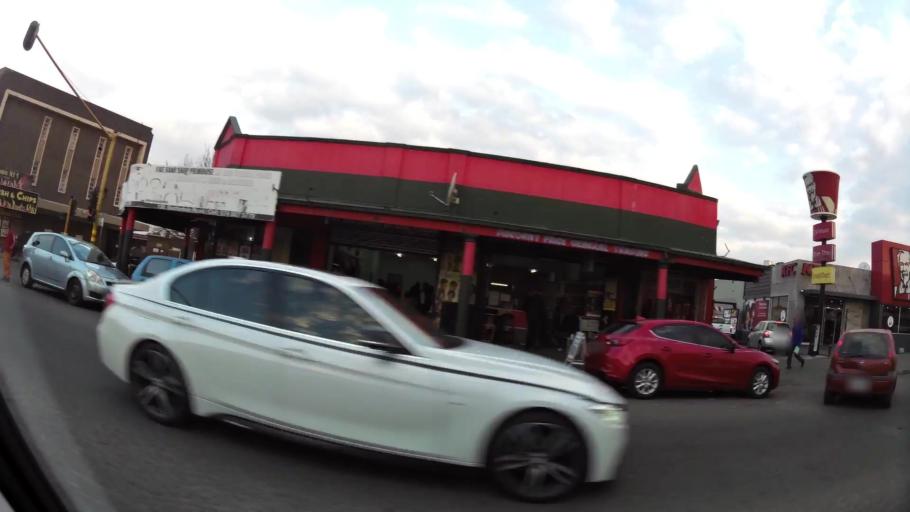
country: ZA
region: Gauteng
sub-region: Ekurhuleni Metropolitan Municipality
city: Germiston
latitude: -26.1888
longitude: 28.1626
